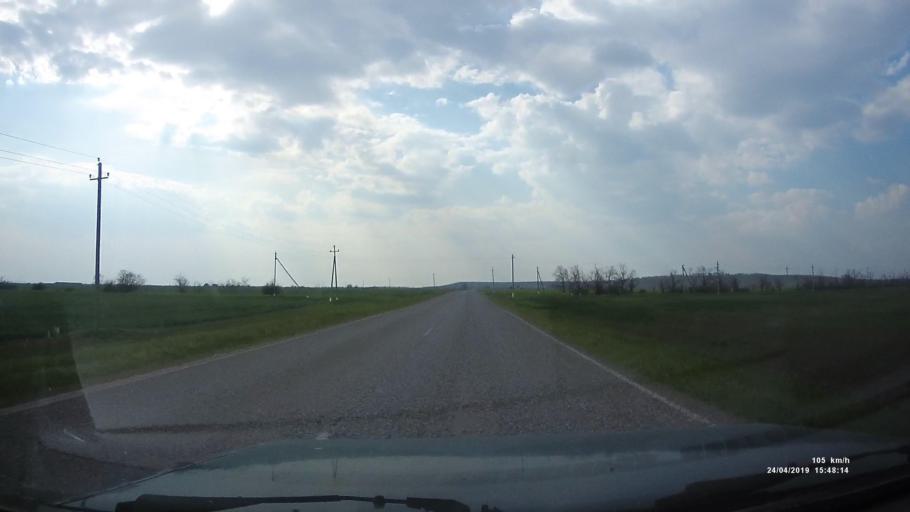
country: RU
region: Kalmykiya
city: Yashalta
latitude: 46.5976
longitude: 42.6801
